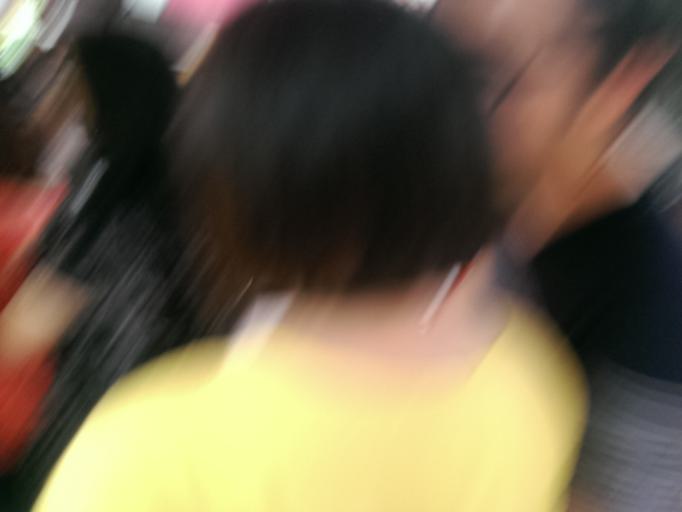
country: TW
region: Taipei
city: Taipei
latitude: 25.0013
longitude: 121.6136
